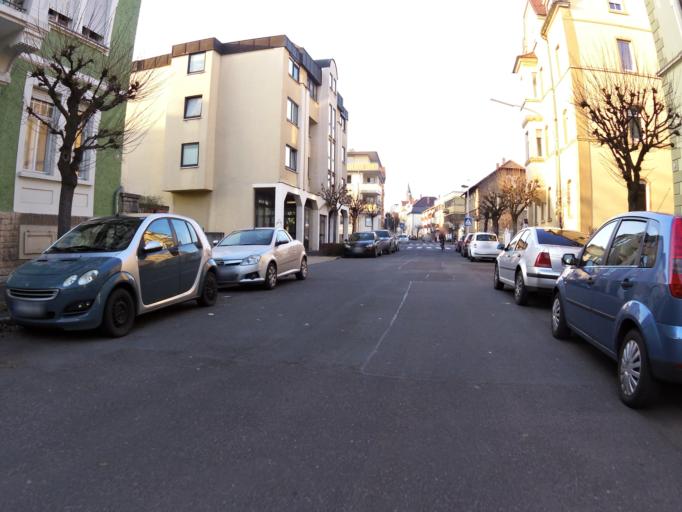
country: DE
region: Bavaria
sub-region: Regierungsbezirk Unterfranken
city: Kitzingen
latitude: 49.7327
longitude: 10.1599
